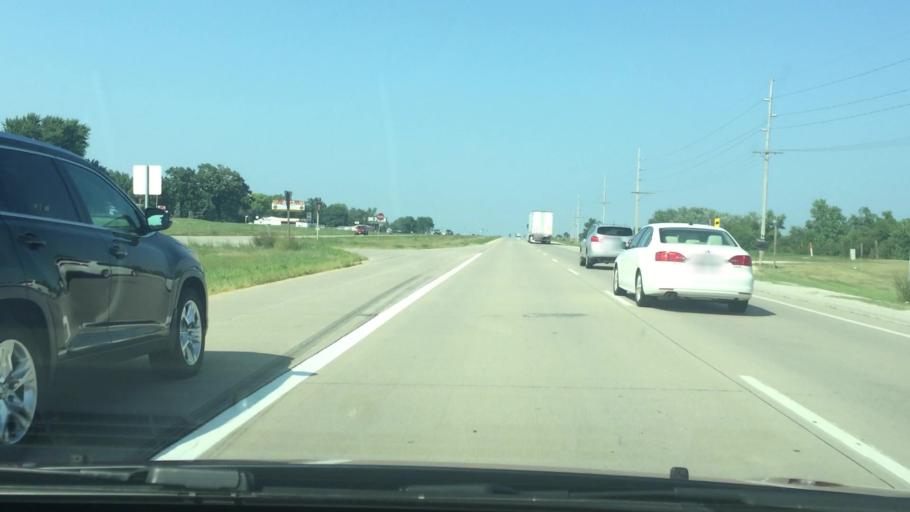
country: US
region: Iowa
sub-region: Muscatine County
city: Muscatine
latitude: 41.4705
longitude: -91.0018
